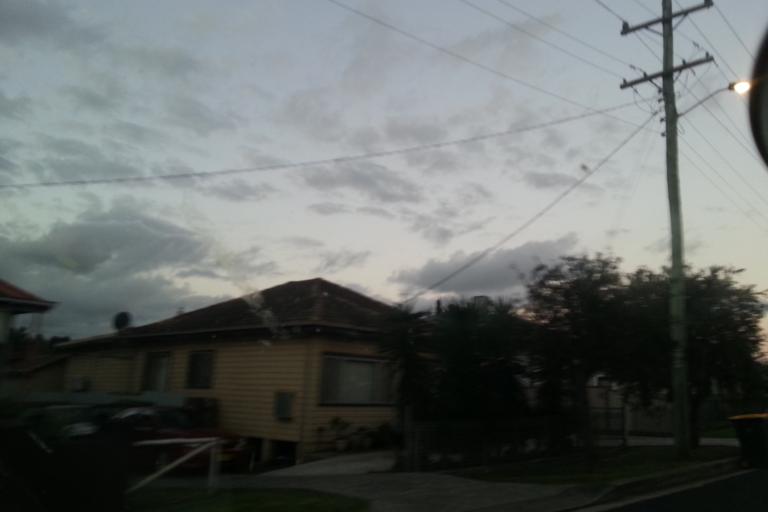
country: AU
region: New South Wales
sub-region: Wollongong
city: Cringila
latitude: -34.4663
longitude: 150.8703
